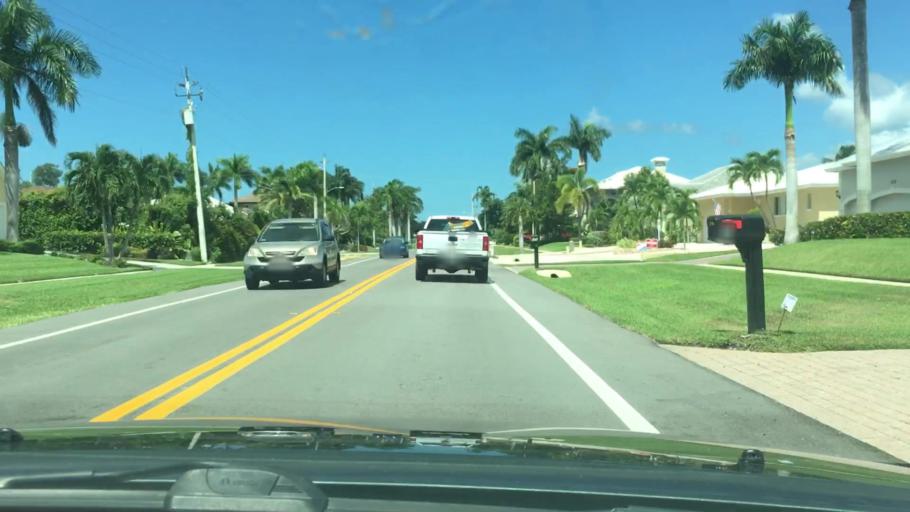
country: US
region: Florida
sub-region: Collier County
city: Marco
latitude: 25.9491
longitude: -81.7358
